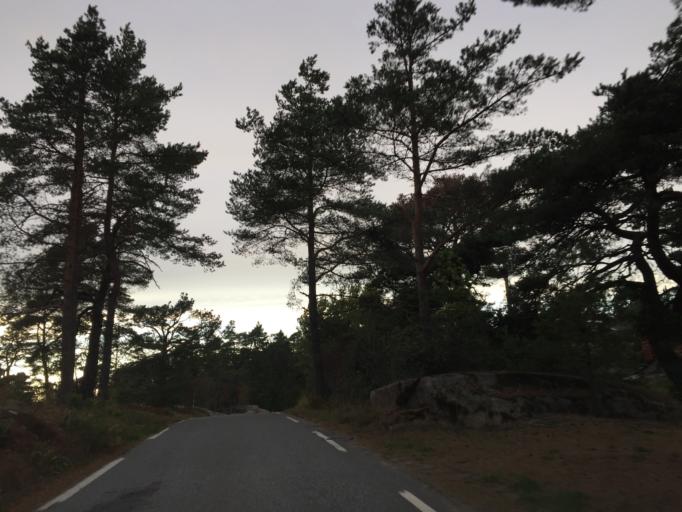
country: NO
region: Ostfold
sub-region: Hvaler
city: Skjaerhalden
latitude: 59.0579
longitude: 11.0087
